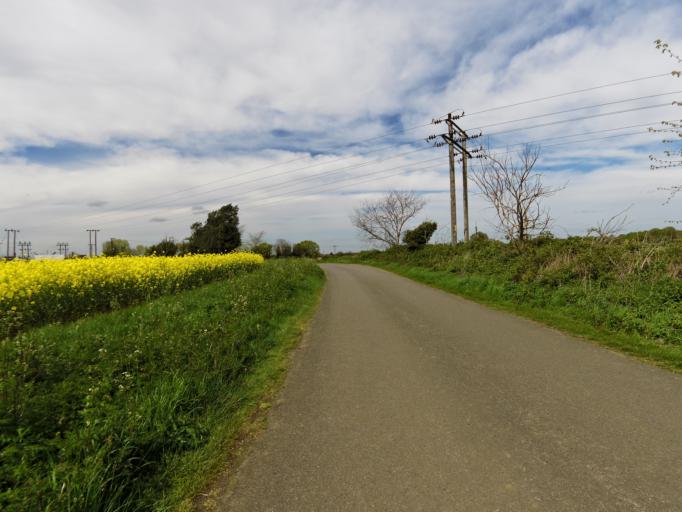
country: GB
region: England
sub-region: Essex
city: Mistley
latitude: 51.9976
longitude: 1.1192
